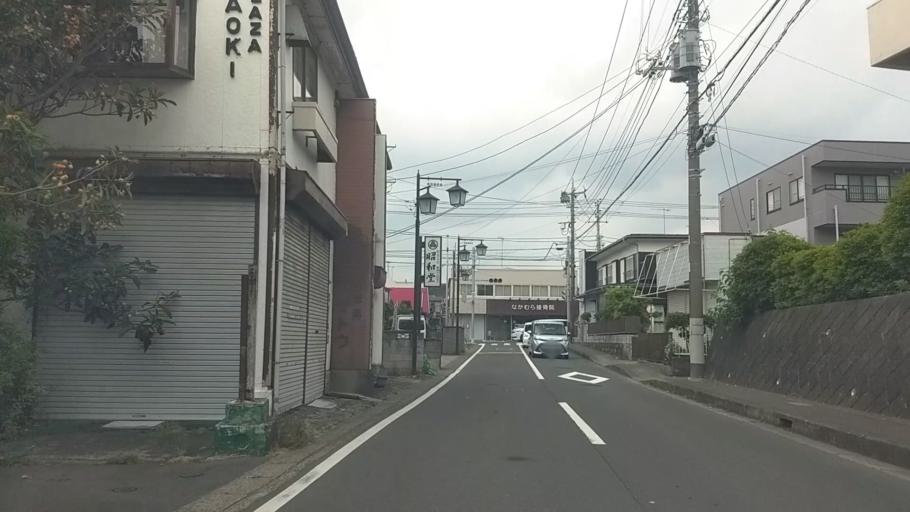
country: JP
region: Kanagawa
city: Atsugi
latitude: 35.4033
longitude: 139.4159
